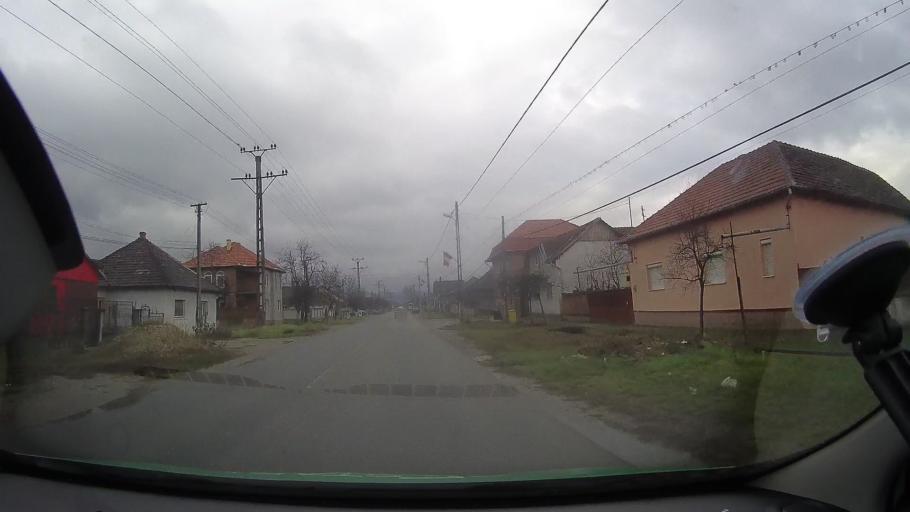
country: RO
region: Arad
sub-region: Comuna Sebis
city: Sebis
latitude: 46.3662
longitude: 22.1309
